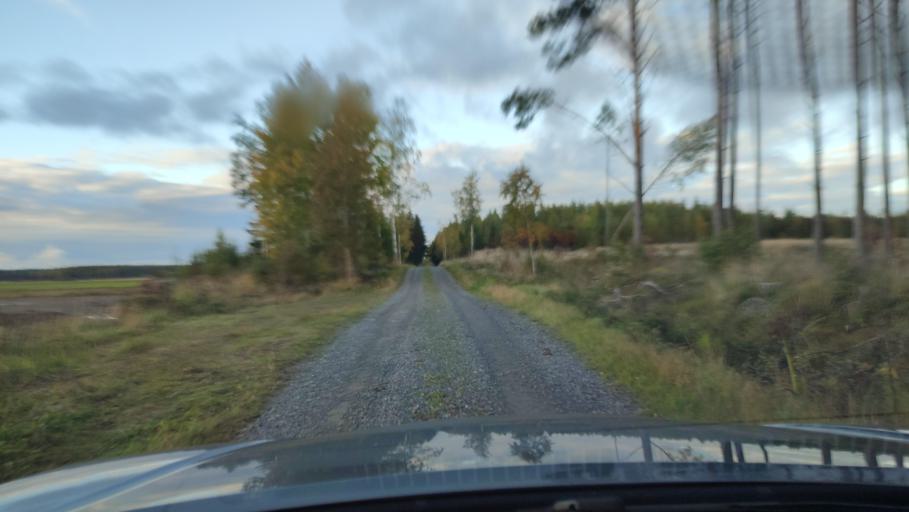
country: FI
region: Ostrobothnia
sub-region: Sydosterbotten
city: Kristinestad
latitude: 62.2487
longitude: 21.4540
